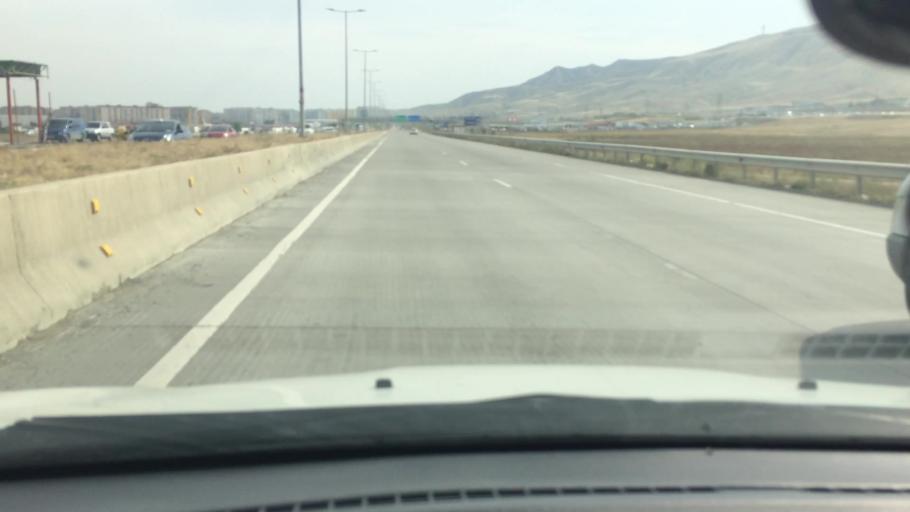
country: GE
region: Kvemo Kartli
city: Rust'avi
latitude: 41.5798
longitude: 44.9540
